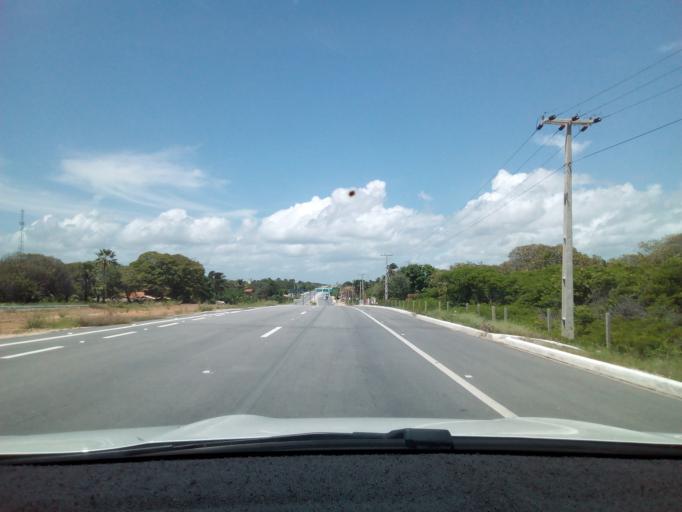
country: BR
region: Ceara
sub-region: Aracati
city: Aracati
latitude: -4.4660
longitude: -37.8015
